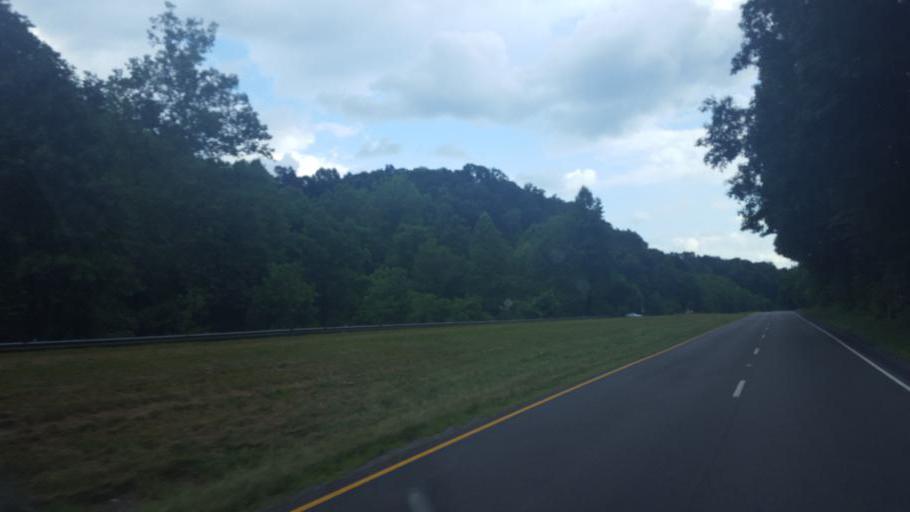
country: US
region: Virginia
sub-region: Wise County
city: Pound
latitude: 37.0788
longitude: -82.5988
